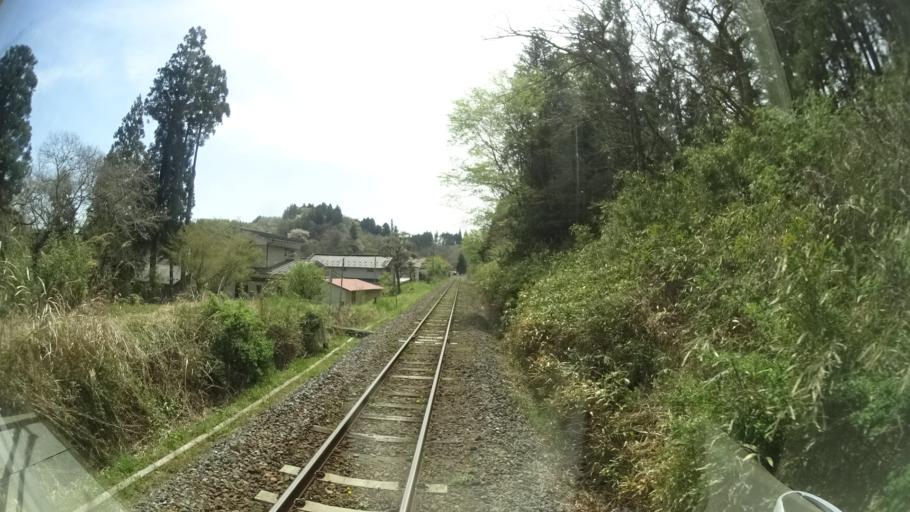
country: JP
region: Iwate
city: Ichinoseki
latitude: 38.9920
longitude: 141.3296
